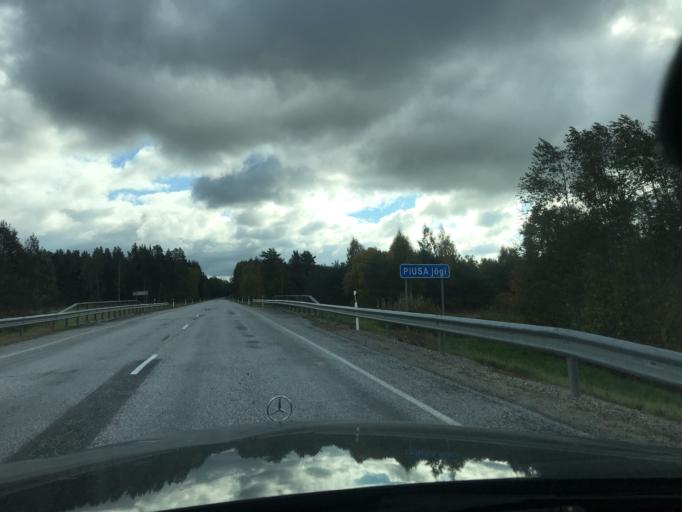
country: EE
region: Vorumaa
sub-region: Voru linn
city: Voru
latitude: 57.7324
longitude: 27.3037
